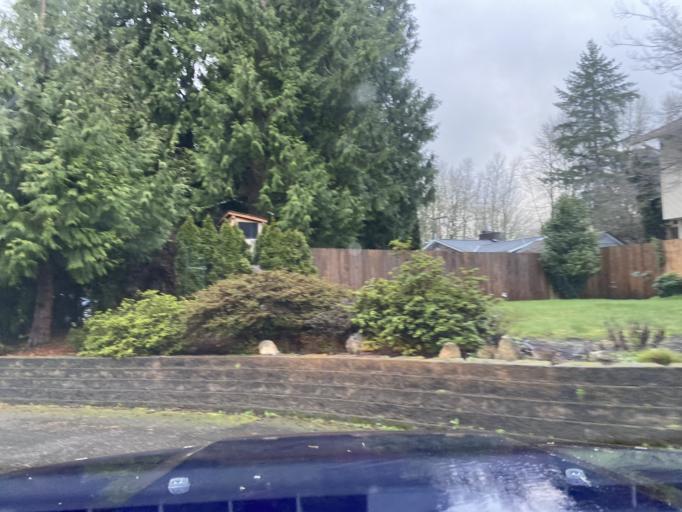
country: US
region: Washington
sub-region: King County
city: Redmond
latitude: 47.6612
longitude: -122.1368
